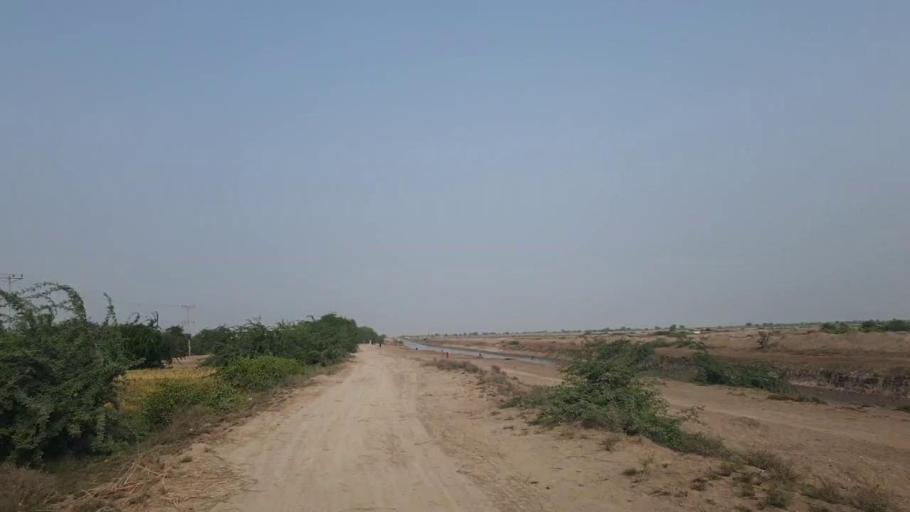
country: PK
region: Sindh
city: Badin
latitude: 24.7160
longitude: 68.7716
